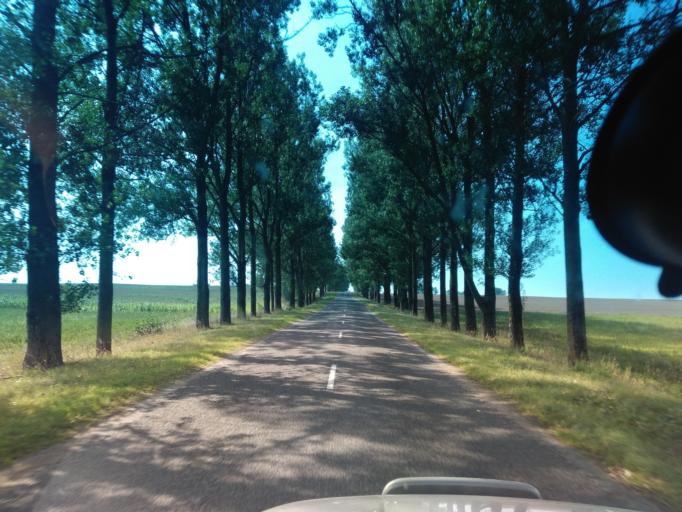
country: BY
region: Minsk
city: Kapyl'
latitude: 53.2666
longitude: 27.1980
